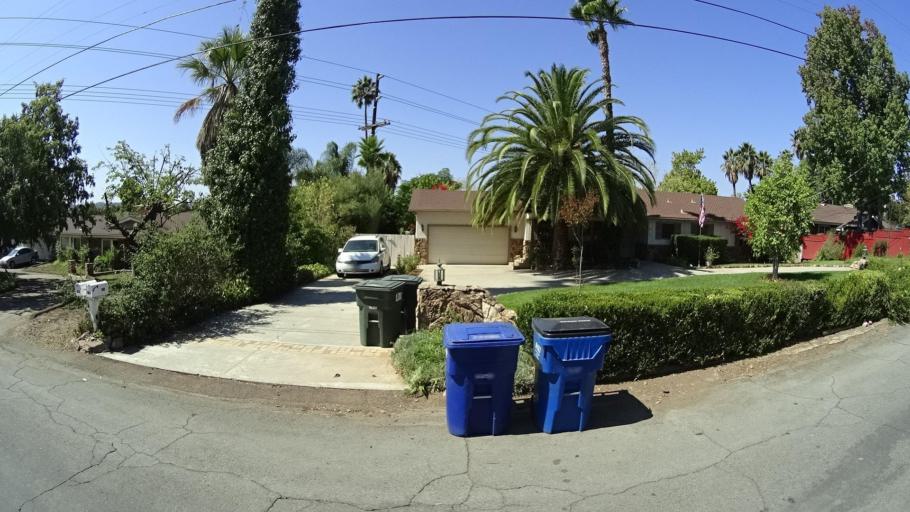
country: US
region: California
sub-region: San Diego County
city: Granite Hills
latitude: 32.8029
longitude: -116.9121
